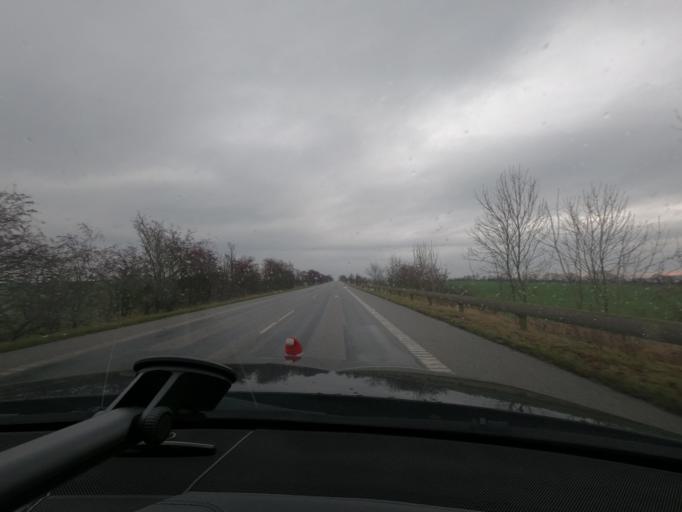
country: DK
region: South Denmark
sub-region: Sonderborg Kommune
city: Horuphav
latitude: 54.8873
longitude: 9.9800
